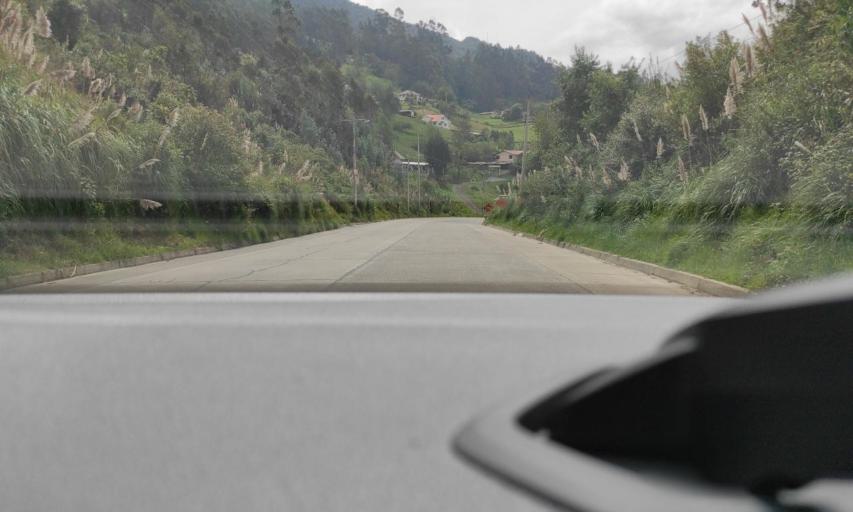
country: EC
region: Canar
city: Azogues
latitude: -2.6883
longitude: -78.8915
